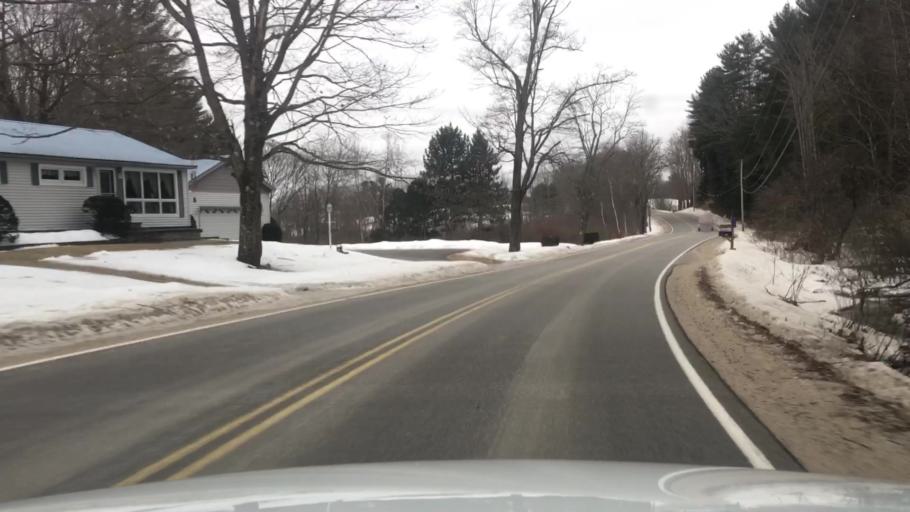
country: US
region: Maine
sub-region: York County
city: Springvale
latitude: 43.5030
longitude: -70.8146
